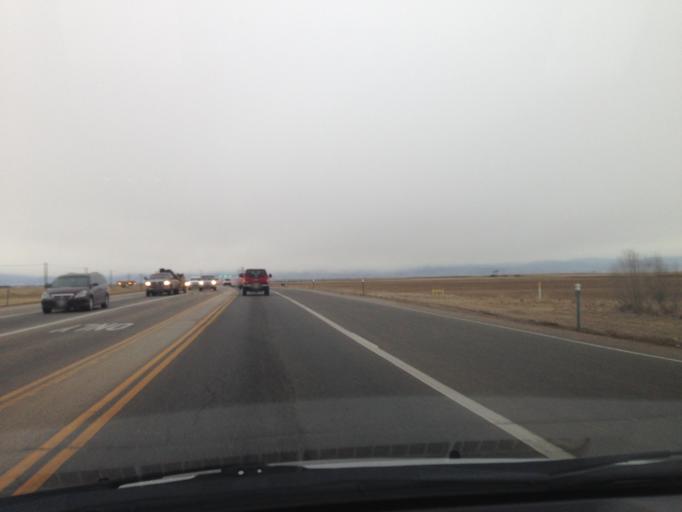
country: US
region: Colorado
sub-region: Weld County
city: Dacono
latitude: 40.0880
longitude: -104.9423
